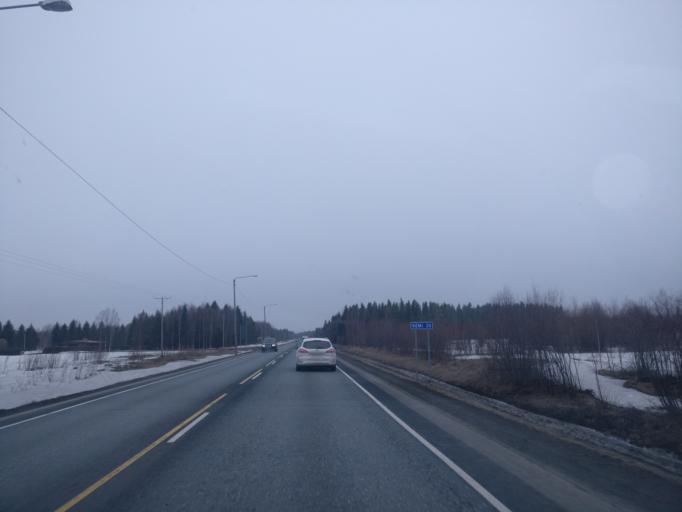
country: FI
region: Lapland
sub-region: Kemi-Tornio
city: Simo
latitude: 65.6702
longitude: 24.9238
